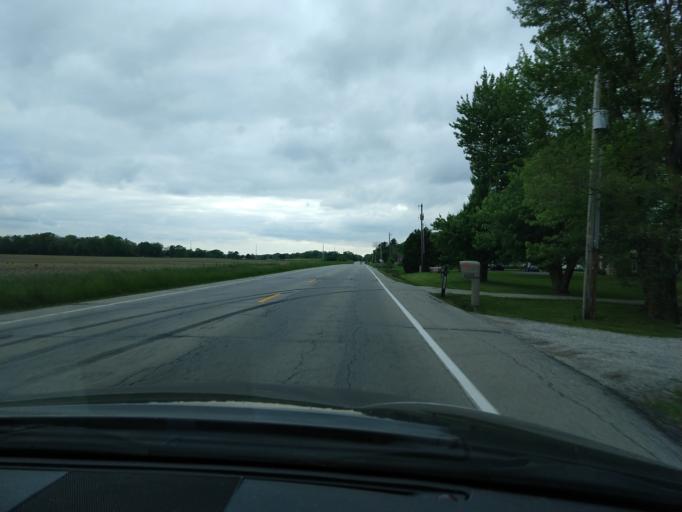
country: US
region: Indiana
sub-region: Madison County
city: Lapel
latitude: 40.0542
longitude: -85.9187
